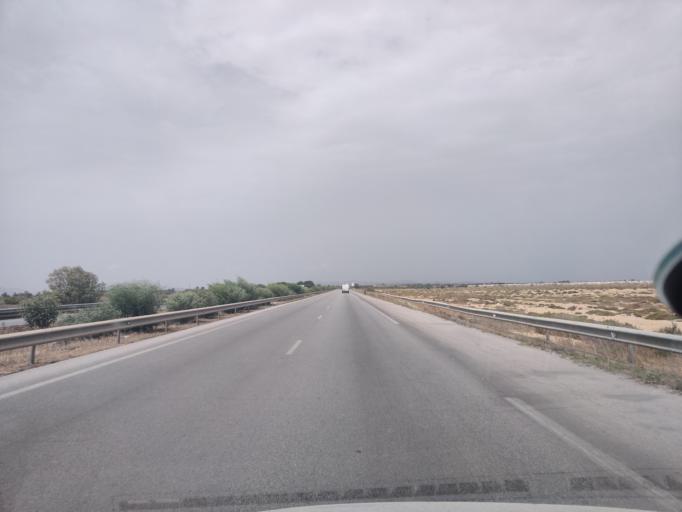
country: TN
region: Susah
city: Harqalah
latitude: 36.0716
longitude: 10.4052
